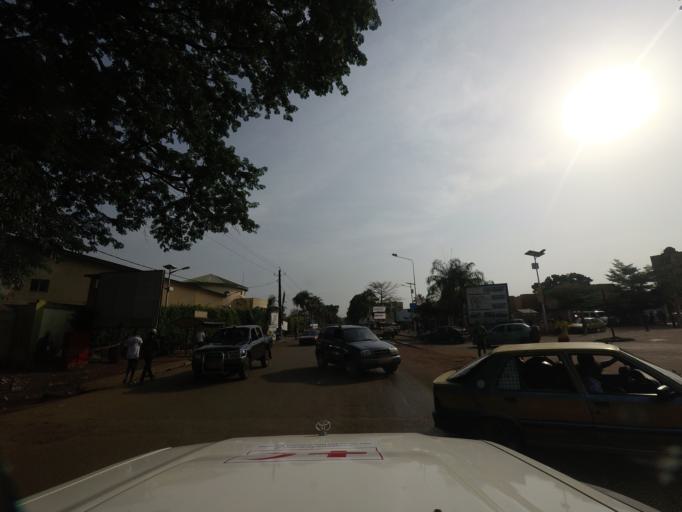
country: GN
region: Conakry
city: Camayenne
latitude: 9.5355
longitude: -13.6850
